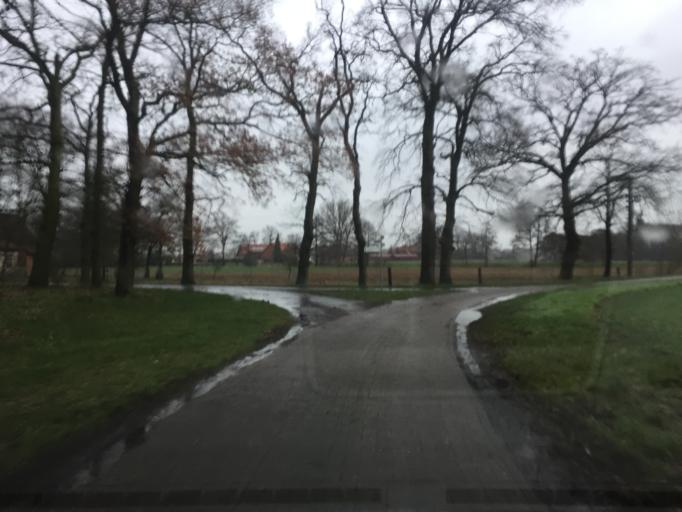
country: DE
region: Lower Saxony
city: Maasen
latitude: 52.6754
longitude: 8.9069
